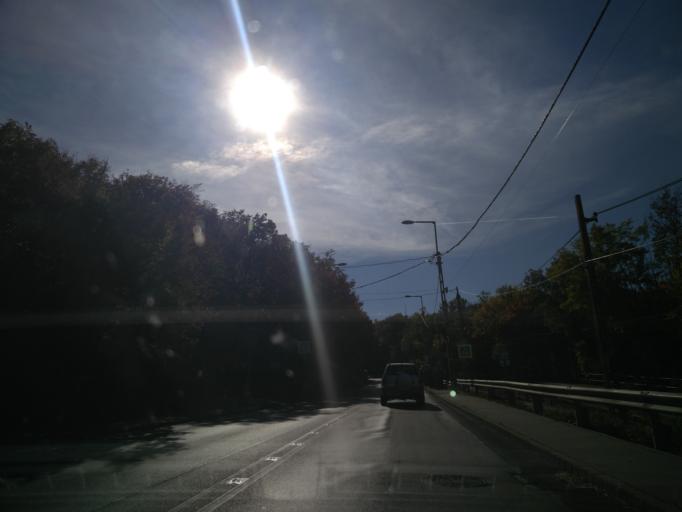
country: HU
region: Budapest
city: Budapest XII. keruelet
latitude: 47.5036
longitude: 18.9904
